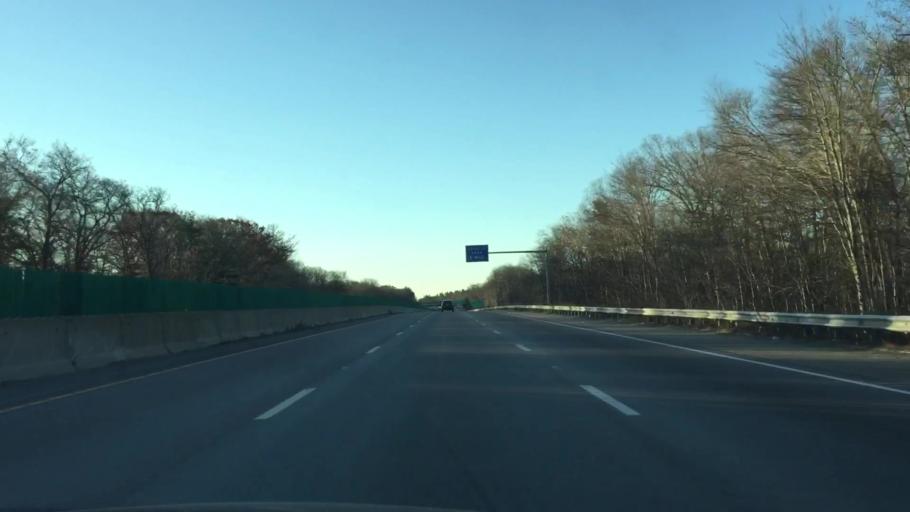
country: US
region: Massachusetts
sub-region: Plymouth County
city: West Bridgewater
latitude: 41.9762
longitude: -71.0261
